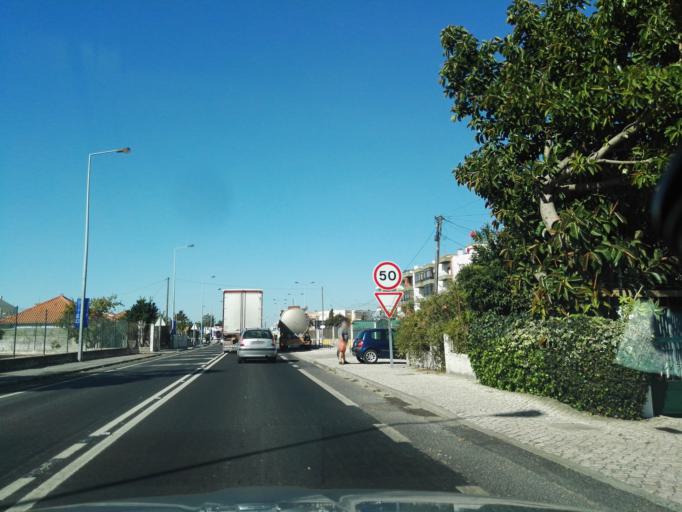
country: PT
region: Santarem
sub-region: Benavente
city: Samora Correia
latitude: 38.9197
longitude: -8.8816
